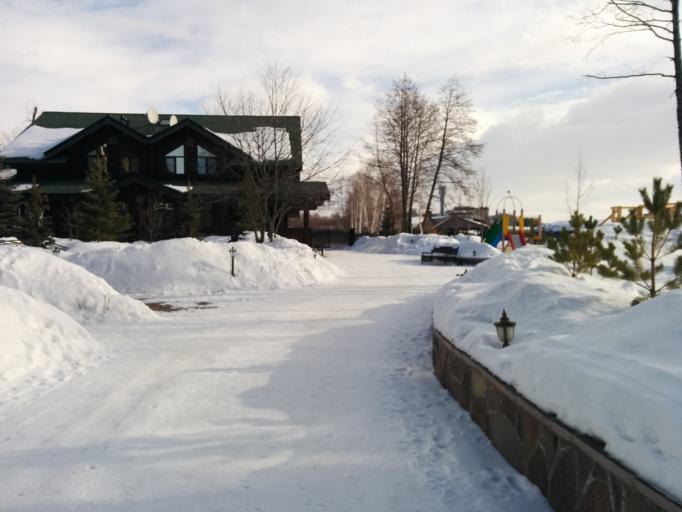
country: RU
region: Bashkortostan
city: Abzakovo
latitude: 53.5955
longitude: 58.6066
